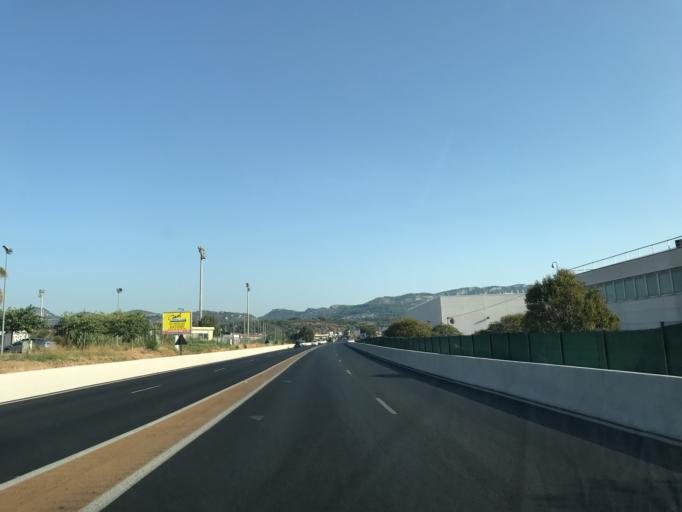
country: FR
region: Provence-Alpes-Cote d'Azur
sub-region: Departement du Var
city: Six-Fours-les-Plages
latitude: 43.1102
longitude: 5.8575
